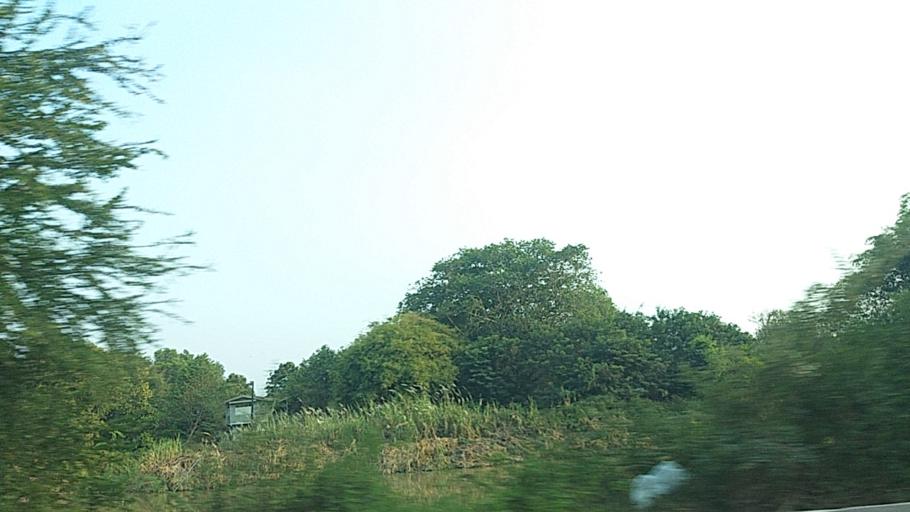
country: TH
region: Nakhon Nayok
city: Ongkharak
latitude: 14.1174
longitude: 100.9912
